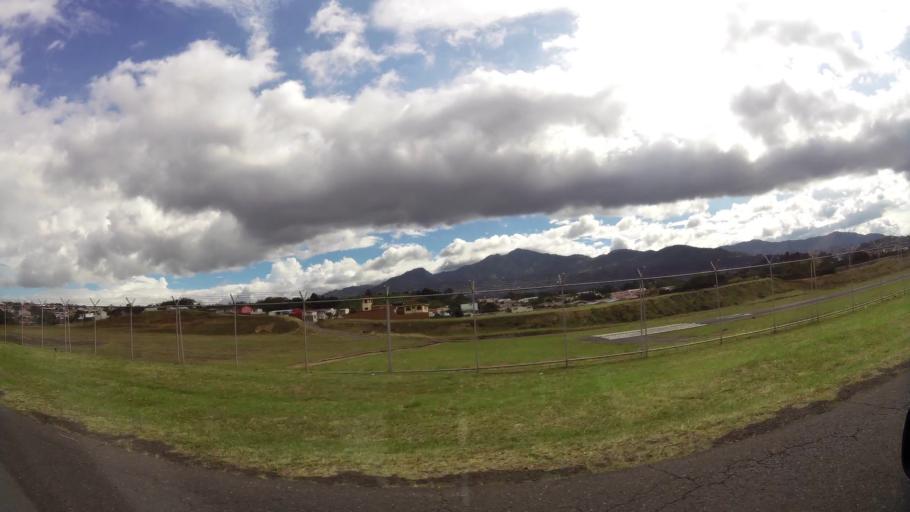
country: CR
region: San Jose
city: San Rafael
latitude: 9.9578
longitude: -84.1323
